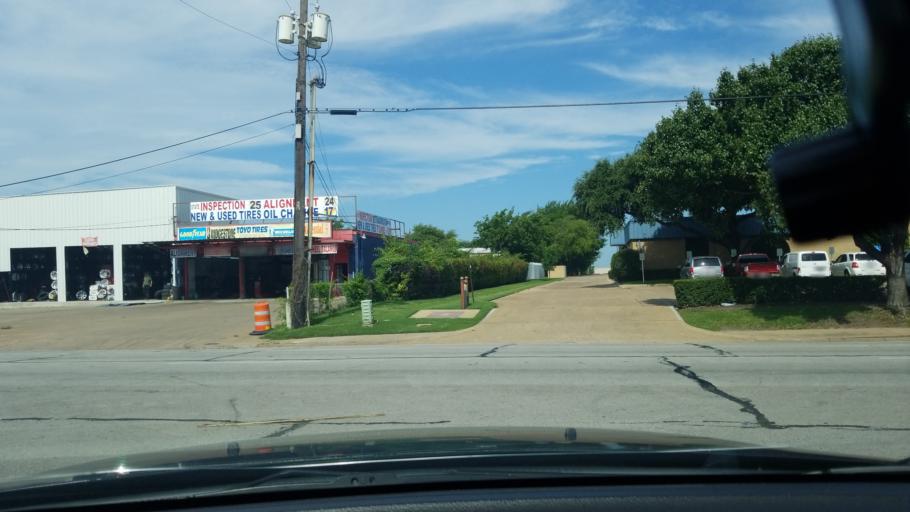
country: US
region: Texas
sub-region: Dallas County
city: Balch Springs
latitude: 32.7711
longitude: -96.6826
